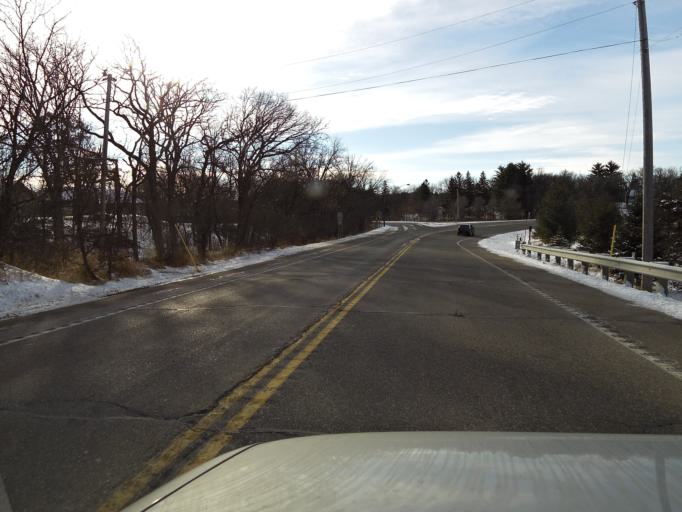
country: US
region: Minnesota
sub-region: Dakota County
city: Inver Grove Heights
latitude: 44.8140
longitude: -93.0854
